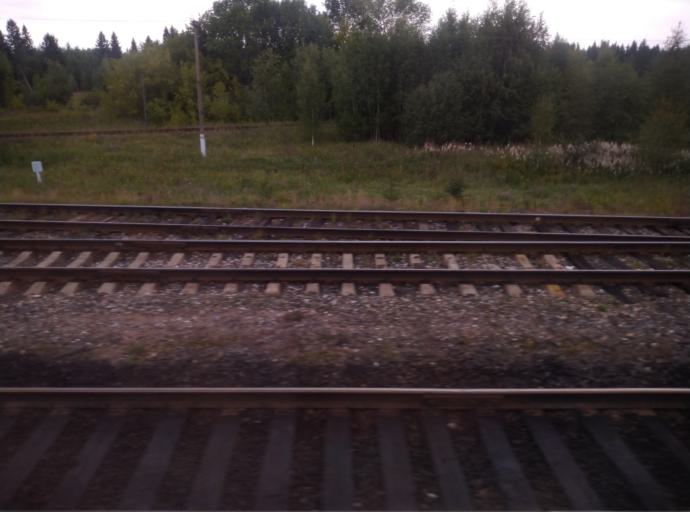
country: RU
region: Jaroslavl
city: Burmakino
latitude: 57.4368
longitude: 40.3285
